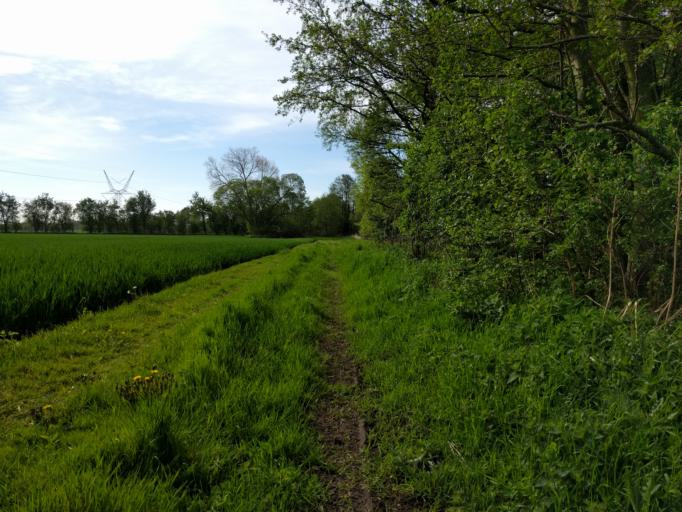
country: DK
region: South Denmark
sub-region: Odense Kommune
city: Bullerup
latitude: 55.4046
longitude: 10.4986
